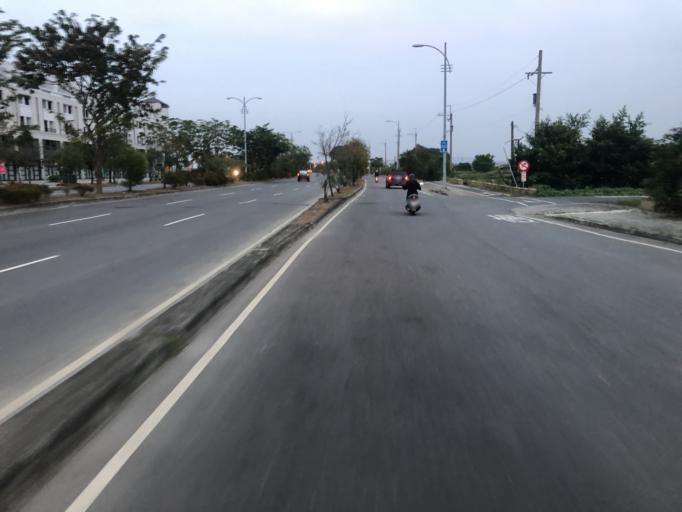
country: TW
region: Taiwan
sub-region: Tainan
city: Tainan
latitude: 23.1079
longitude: 120.3054
